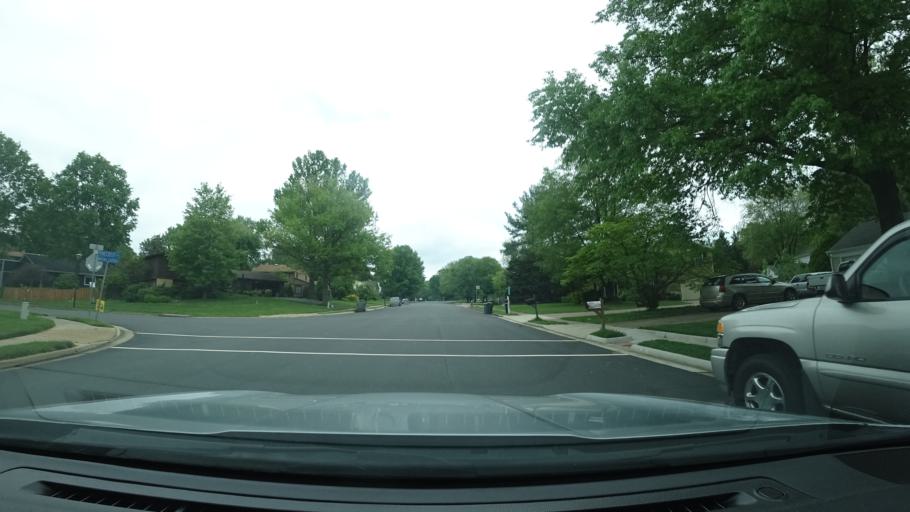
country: US
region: Virginia
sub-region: Fairfax County
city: Oak Hill
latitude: 38.9324
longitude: -77.3817
